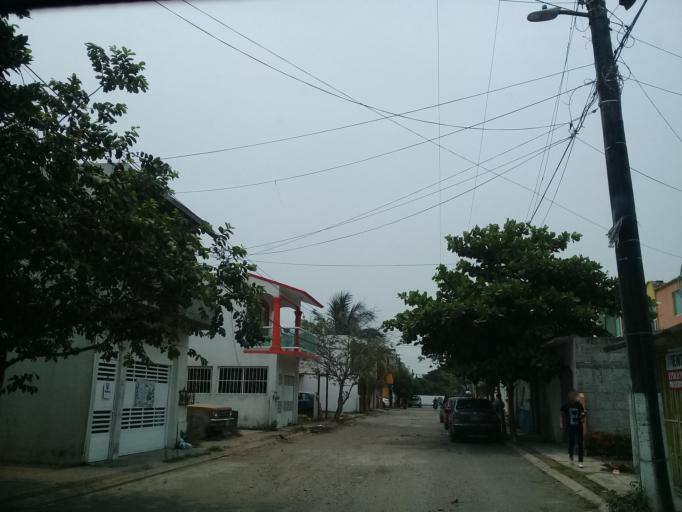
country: MX
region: Veracruz
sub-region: Veracruz
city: Las Amapolas
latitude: 19.1523
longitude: -96.2036
